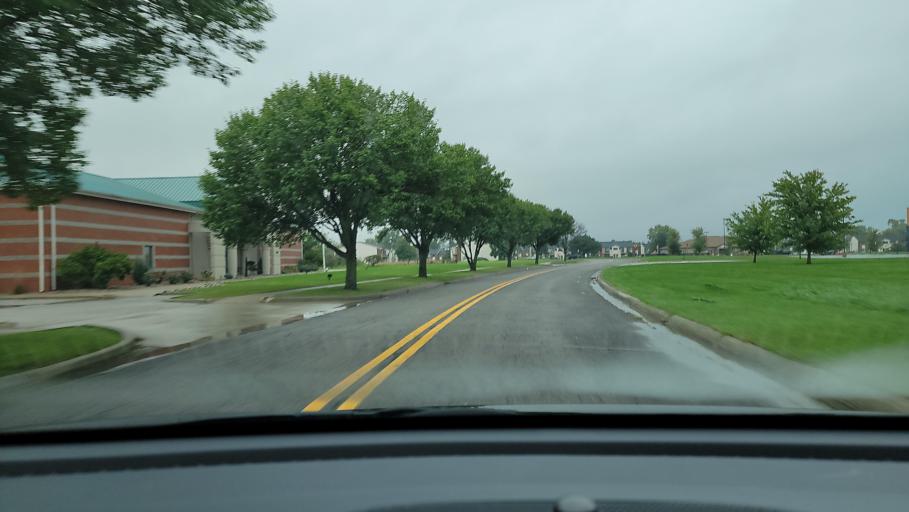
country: US
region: Indiana
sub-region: Porter County
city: South Haven
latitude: 41.5527
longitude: -87.1619
